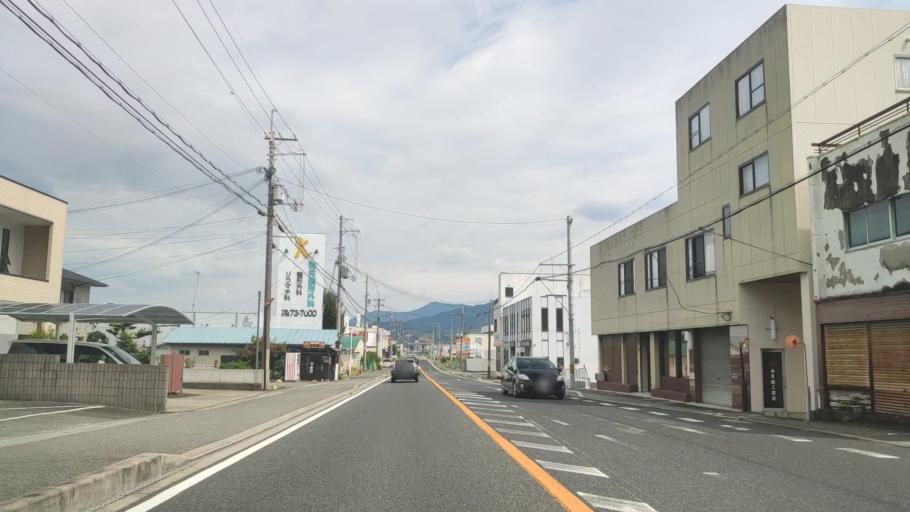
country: JP
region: Wakayama
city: Iwade
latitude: 34.2689
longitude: 135.4084
